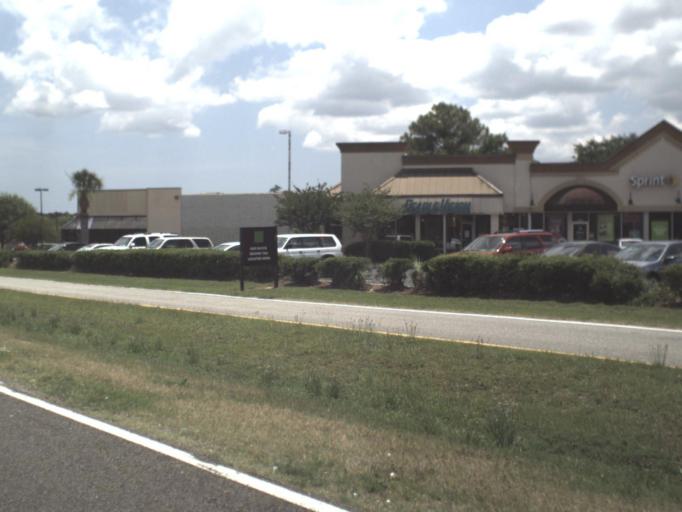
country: US
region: Florida
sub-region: Duval County
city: Jacksonville
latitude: 30.3217
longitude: -81.5550
